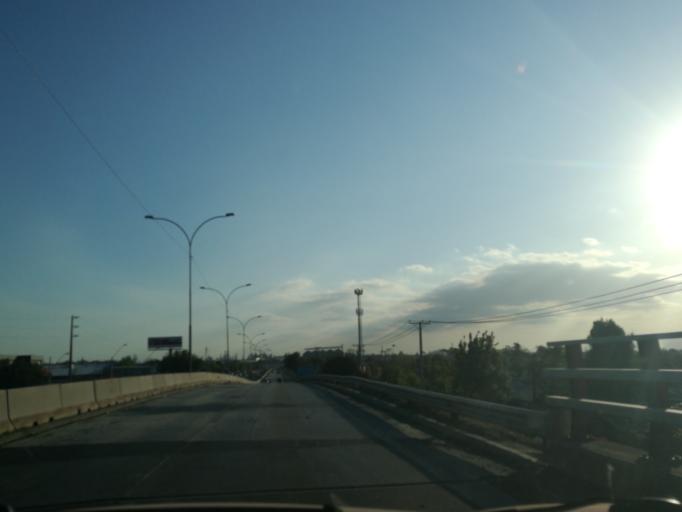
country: CL
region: O'Higgins
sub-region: Provincia de Cachapoal
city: Rancagua
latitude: -34.1790
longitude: -70.7332
